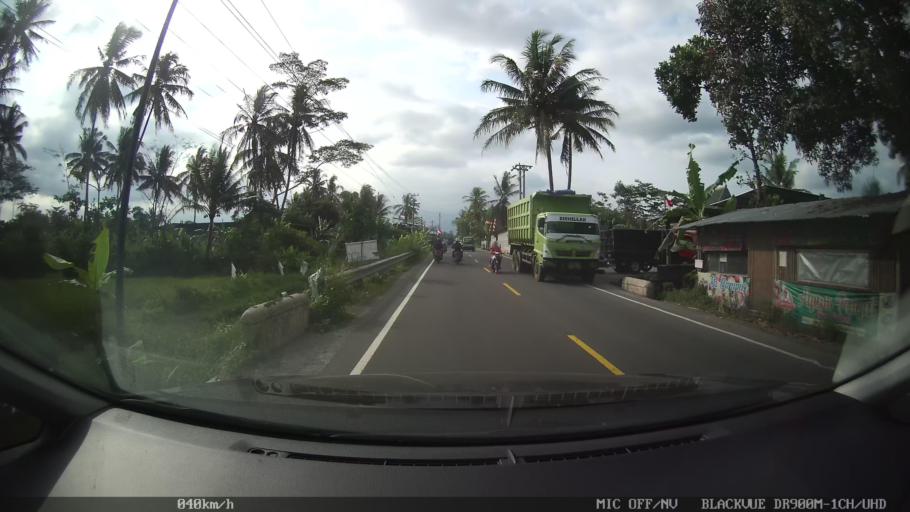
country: ID
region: Central Java
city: Candi Prambanan
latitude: -7.6872
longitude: 110.4611
